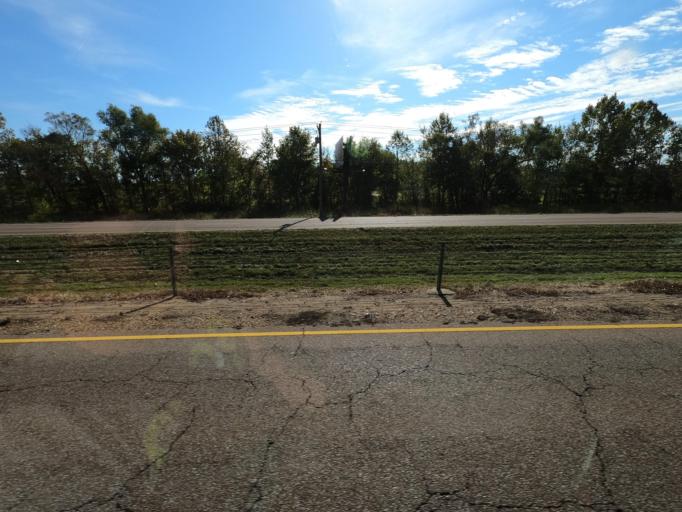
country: US
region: Tennessee
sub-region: Tipton County
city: Brighton
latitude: 35.5054
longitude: -89.7149
